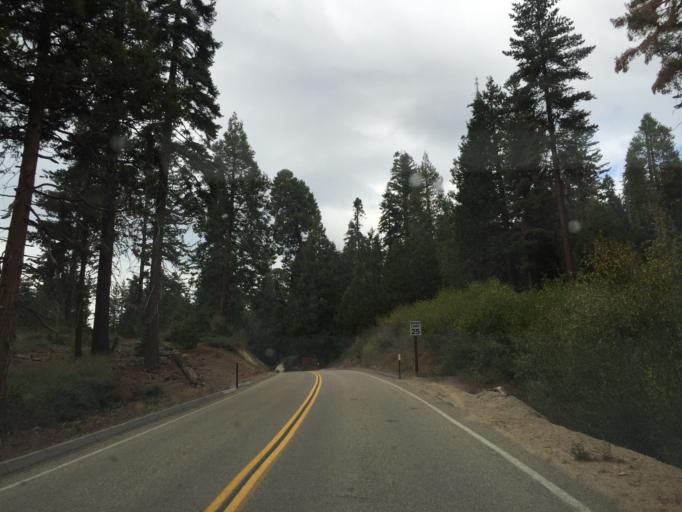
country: US
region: California
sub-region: Tulare County
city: Three Rivers
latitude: 36.7205
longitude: -118.9544
